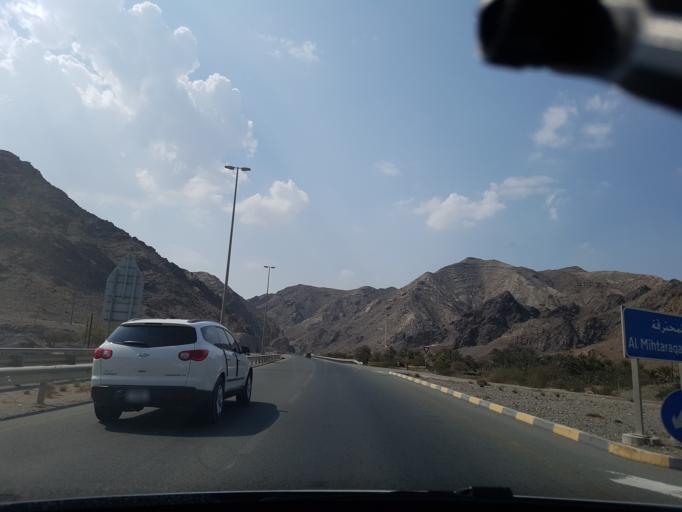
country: AE
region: Al Fujayrah
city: Dibba Al-Fujairah
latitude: 25.5335
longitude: 56.1319
